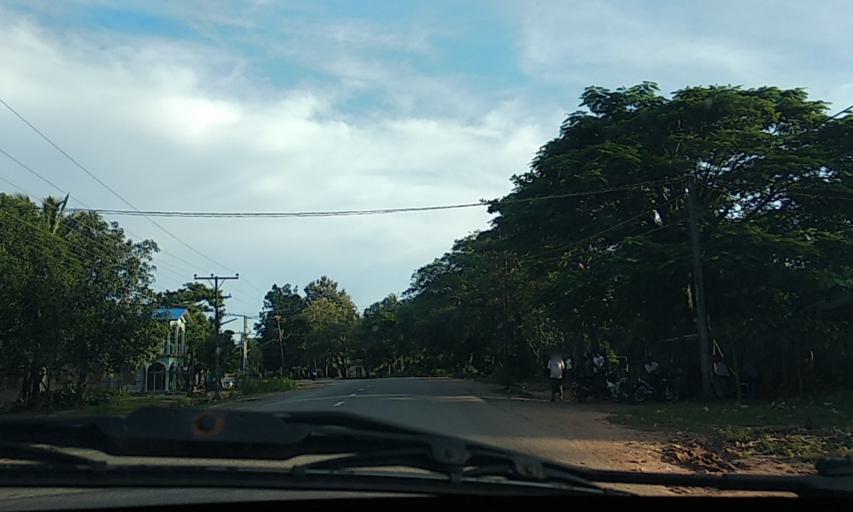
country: MM
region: Mon
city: Mawlamyine
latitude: 16.3994
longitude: 97.7023
